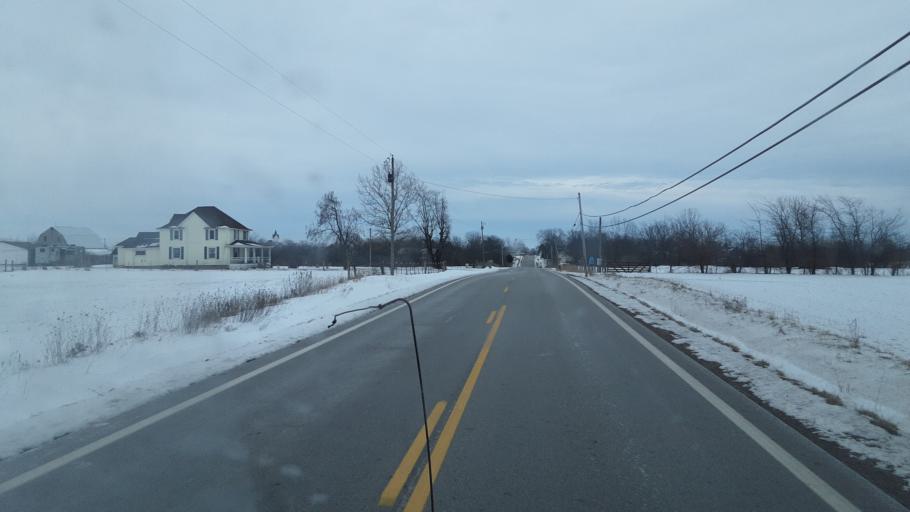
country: US
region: Ohio
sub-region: Madison County
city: Mount Sterling
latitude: 39.6762
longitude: -83.1868
